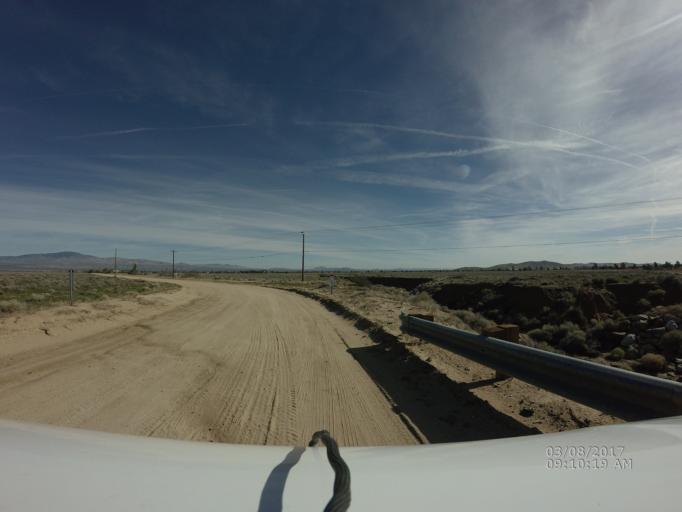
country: US
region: California
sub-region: Los Angeles County
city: Green Valley
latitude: 34.7461
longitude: -118.4666
